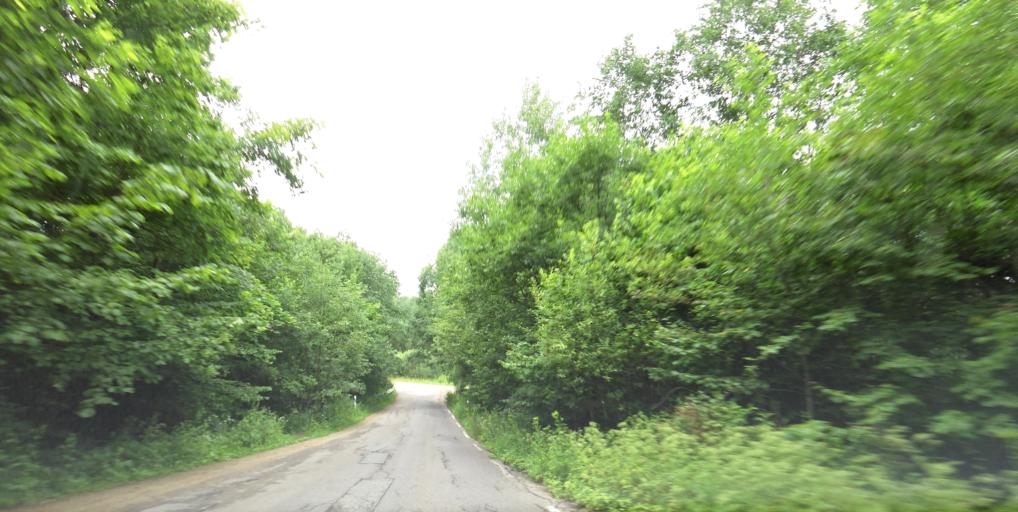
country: LT
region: Vilnius County
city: Pilaite
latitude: 54.6969
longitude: 25.1920
